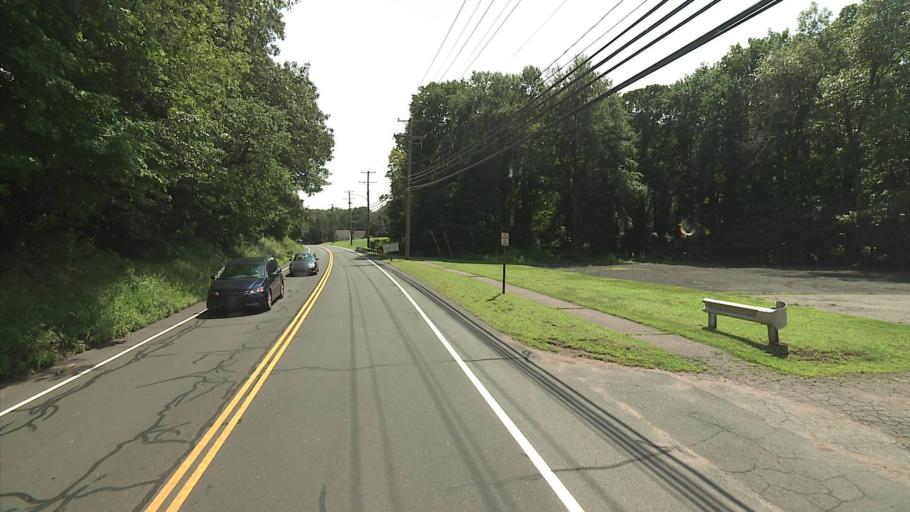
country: US
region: Connecticut
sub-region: Tolland County
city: Rockville
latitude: 41.8582
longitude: -72.4673
